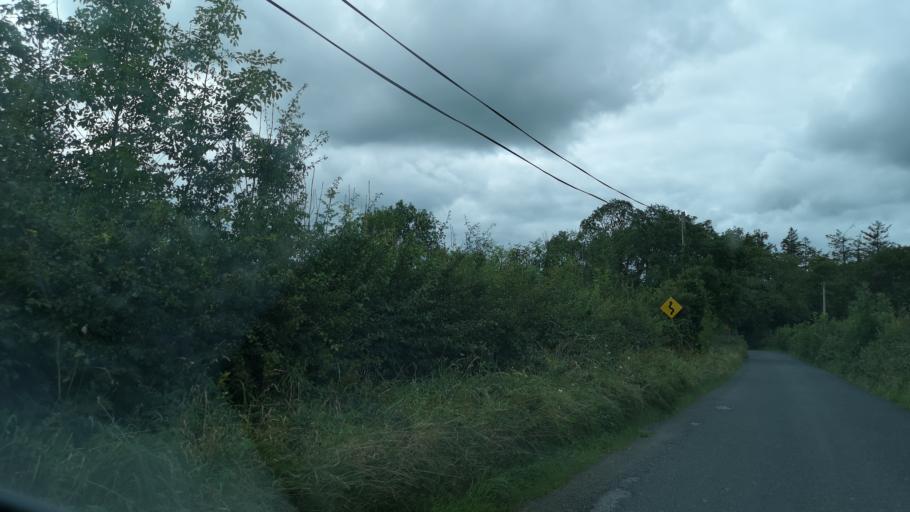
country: IE
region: Connaught
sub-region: County Galway
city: Loughrea
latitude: 53.1625
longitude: -8.4667
